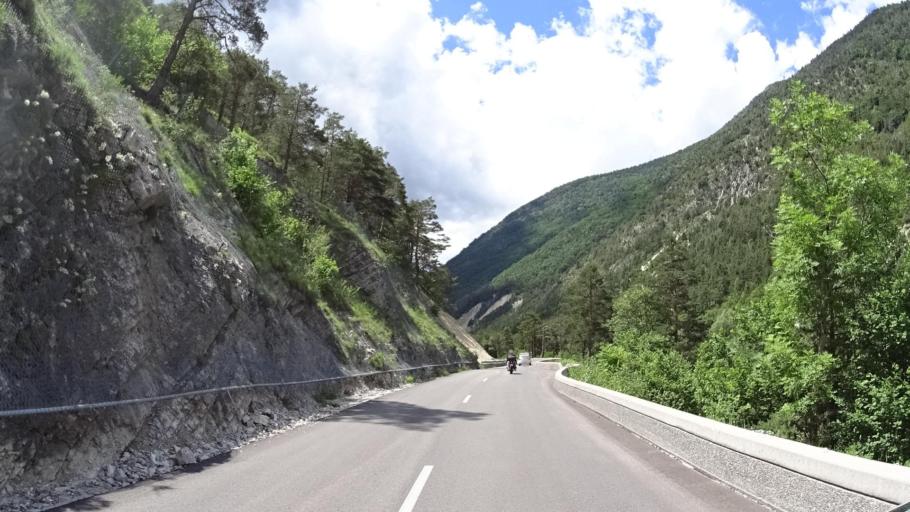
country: FR
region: Provence-Alpes-Cote d'Azur
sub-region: Departement des Alpes-de-Haute-Provence
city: Annot
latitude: 44.0517
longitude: 6.5718
